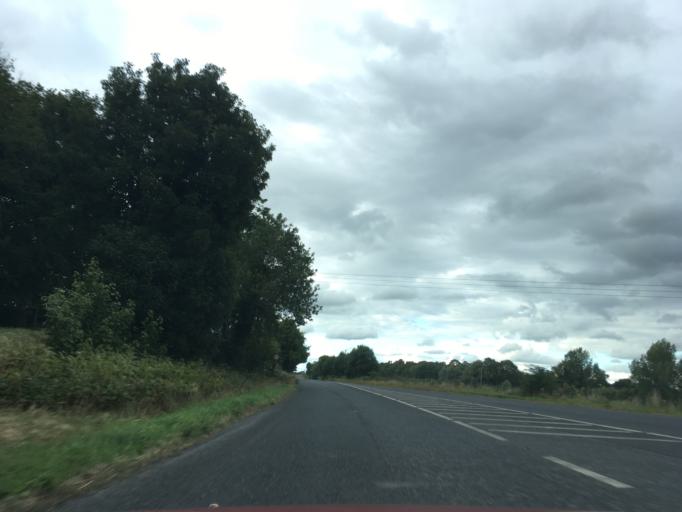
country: IE
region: Munster
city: Cahir
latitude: 52.4030
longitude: -7.8969
